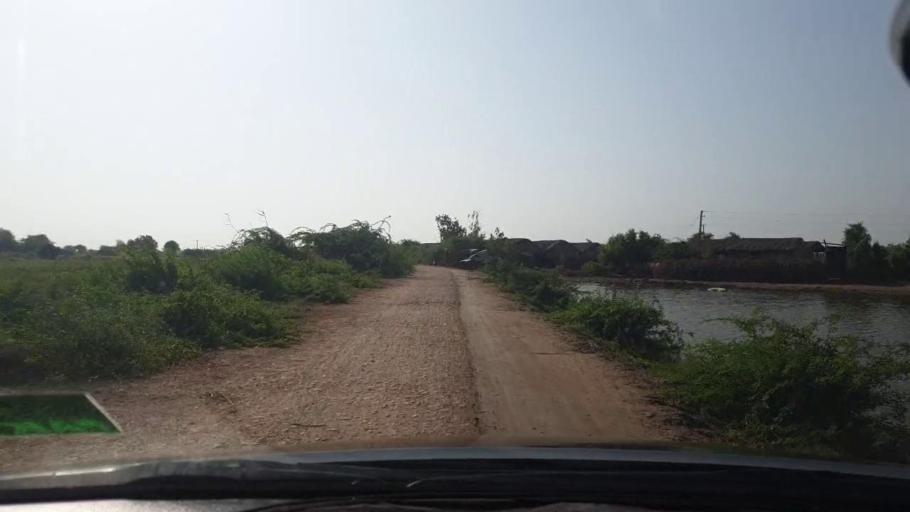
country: PK
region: Sindh
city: Tando Bago
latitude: 24.7197
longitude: 68.9607
